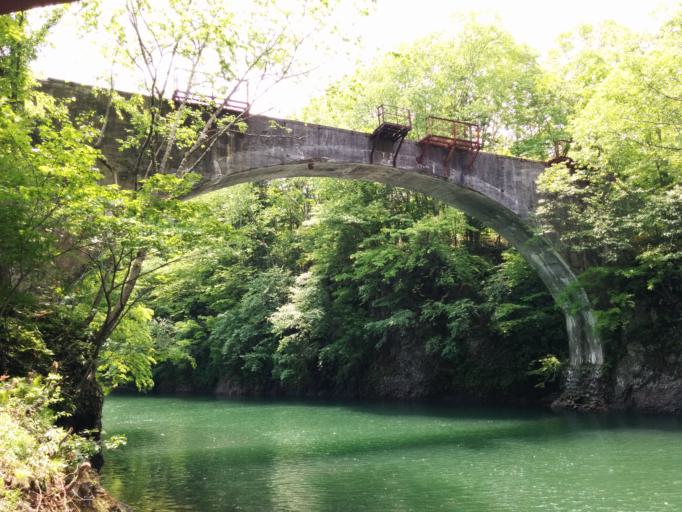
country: JP
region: Hokkaido
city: Otofuke
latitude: 43.3552
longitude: 143.2594
